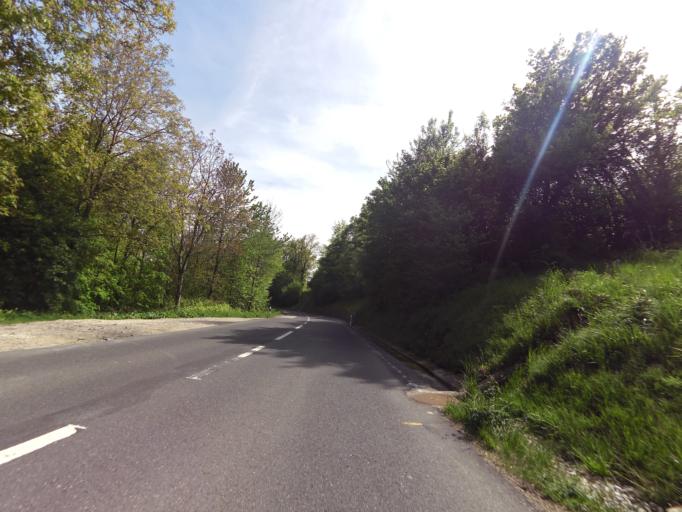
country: CH
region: Vaud
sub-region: Nyon District
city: Genolier
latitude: 46.4478
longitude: 6.2198
